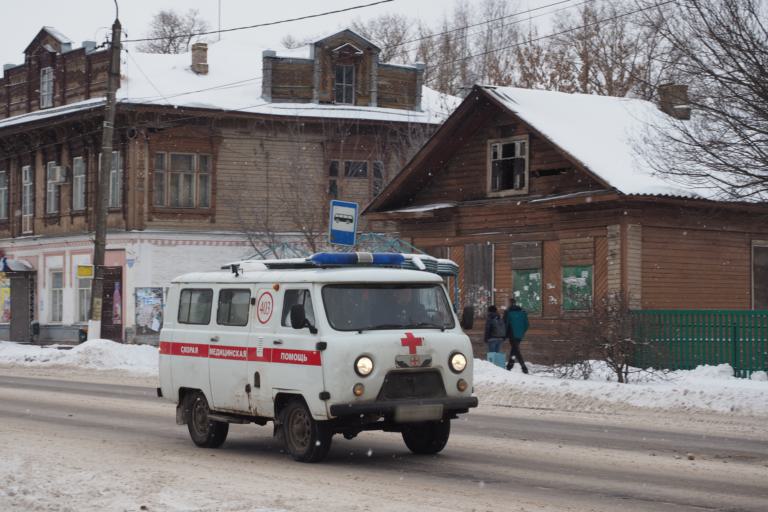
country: RU
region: Tverskaya
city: Bezhetsk
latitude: 57.7879
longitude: 36.6909
